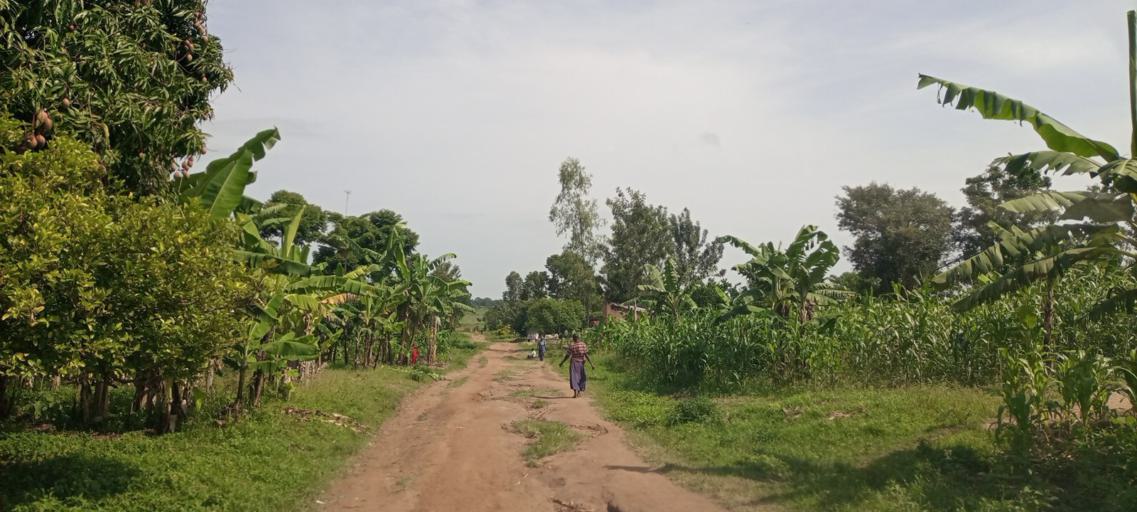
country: UG
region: Eastern Region
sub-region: Budaka District
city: Budaka
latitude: 1.1366
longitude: 34.0150
